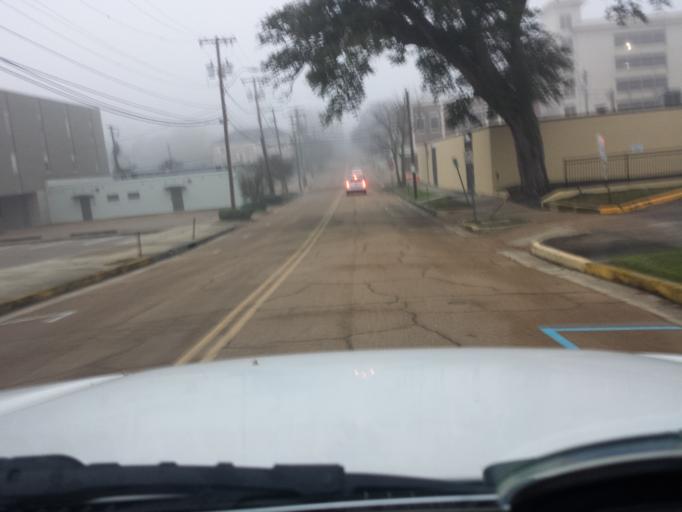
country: US
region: Mississippi
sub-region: Hinds County
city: Jackson
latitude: 32.3014
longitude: -90.1804
